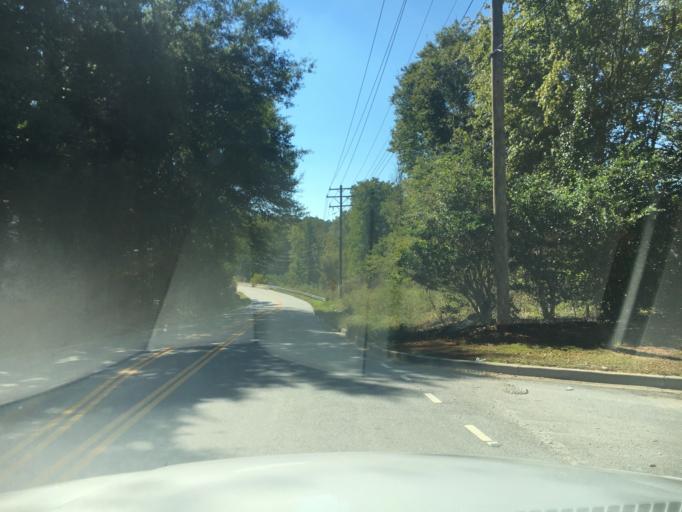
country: US
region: South Carolina
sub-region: Greenville County
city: Wade Hampton
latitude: 34.8554
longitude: -82.3006
